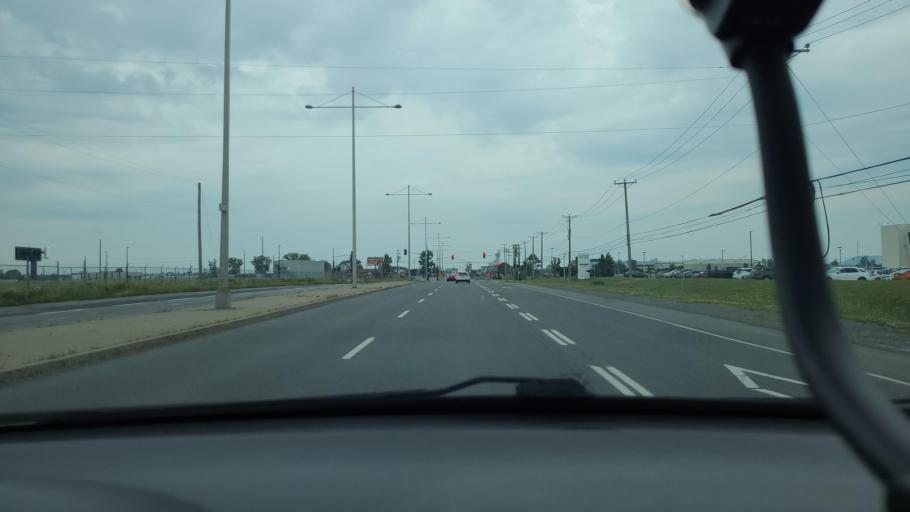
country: CA
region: Quebec
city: Dorval
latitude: 45.4796
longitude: -73.7264
